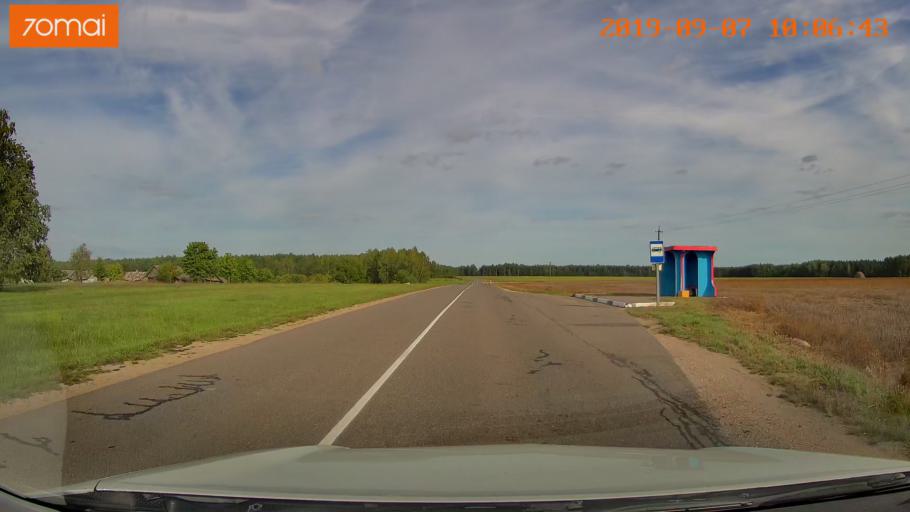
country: BY
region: Grodnenskaya
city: Voranava
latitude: 54.0659
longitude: 25.4020
